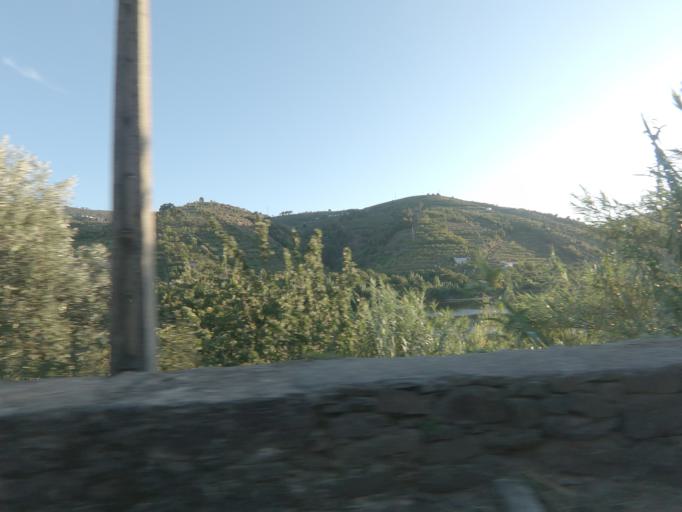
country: PT
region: Vila Real
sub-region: Mesao Frio
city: Mesao Frio
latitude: 41.1589
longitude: -7.8576
